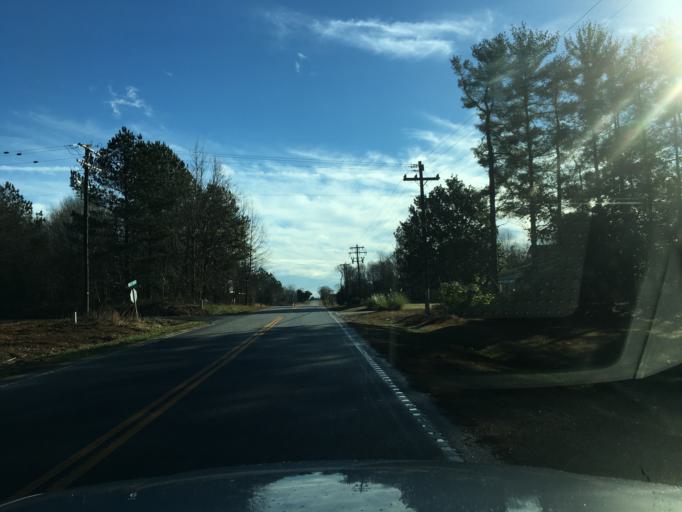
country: US
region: South Carolina
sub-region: Spartanburg County
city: Cowpens
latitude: 35.0100
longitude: -81.8694
